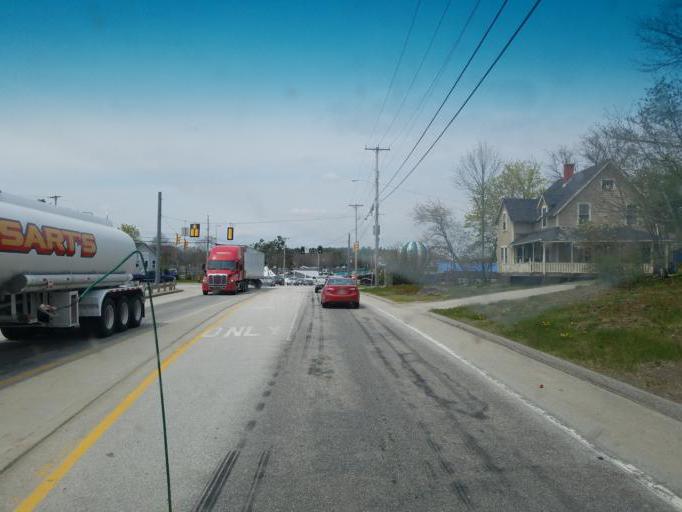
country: US
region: Maine
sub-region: Hancock County
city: Ellsworth
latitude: 44.5497
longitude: -68.4259
